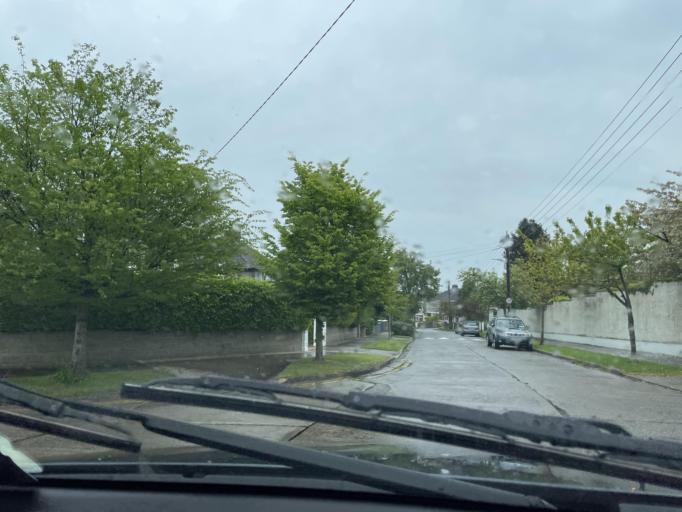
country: IE
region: Leinster
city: Dundrum
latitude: 53.2907
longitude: -6.2523
